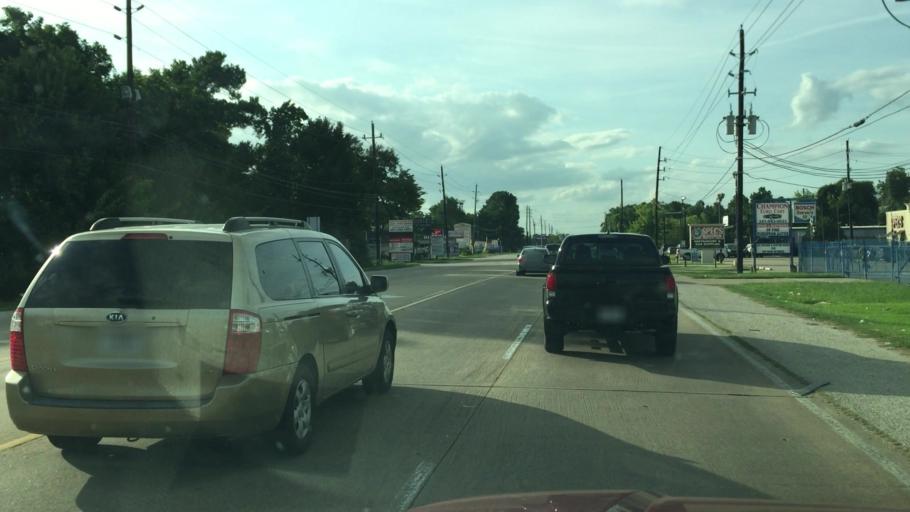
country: US
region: Texas
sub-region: Harris County
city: Hudson
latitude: 29.9893
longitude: -95.4994
